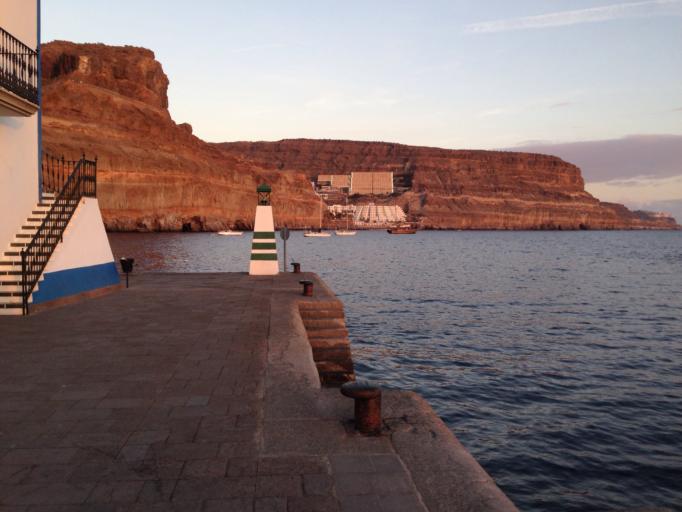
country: ES
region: Canary Islands
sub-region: Provincia de Las Palmas
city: Puerto Rico
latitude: 27.8165
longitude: -15.7641
